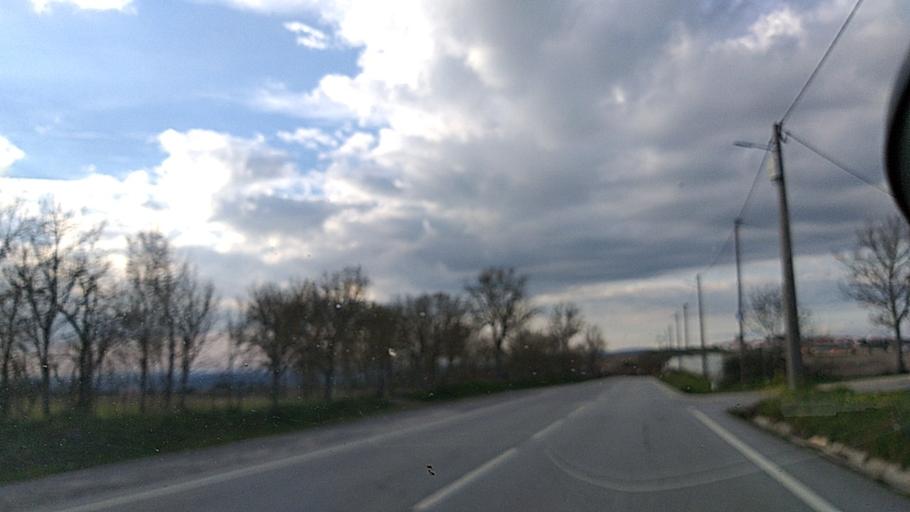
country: ES
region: Castille and Leon
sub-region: Provincia de Salamanca
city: Aldea del Obispo
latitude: 40.7132
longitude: -6.8993
